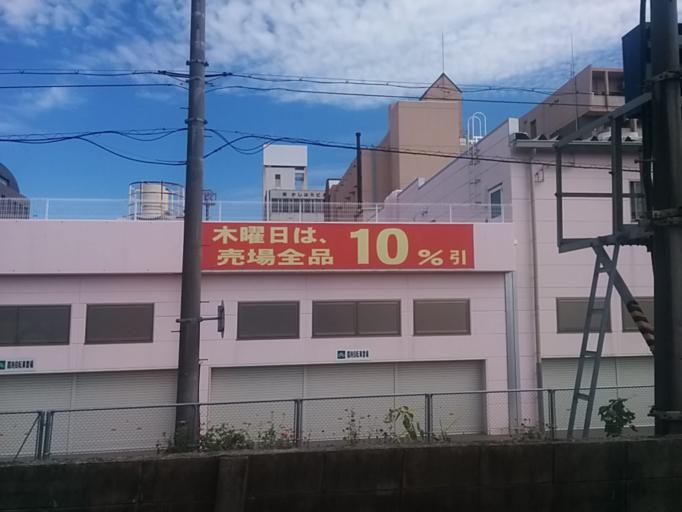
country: JP
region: Nara
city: Kashihara-shi
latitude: 34.5101
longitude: 135.7910
